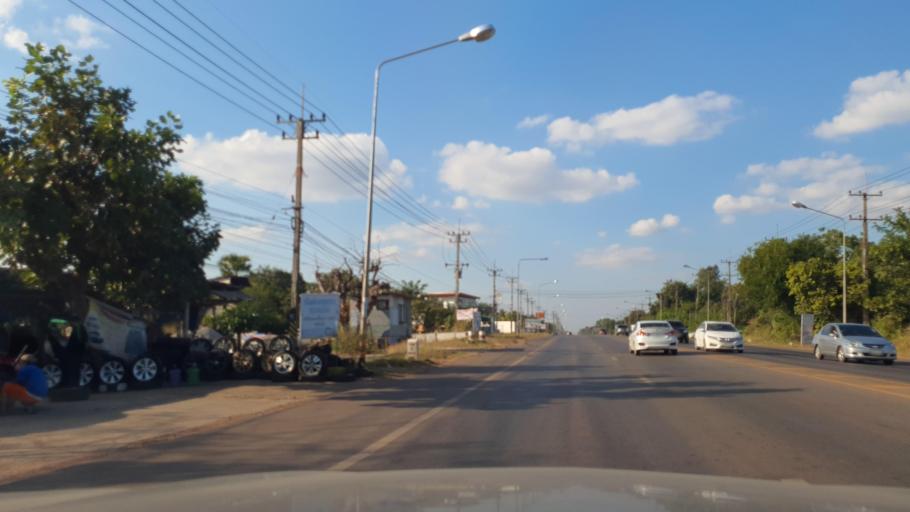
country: TH
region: Sakon Nakhon
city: Sakon Nakhon
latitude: 17.1662
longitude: 104.1006
